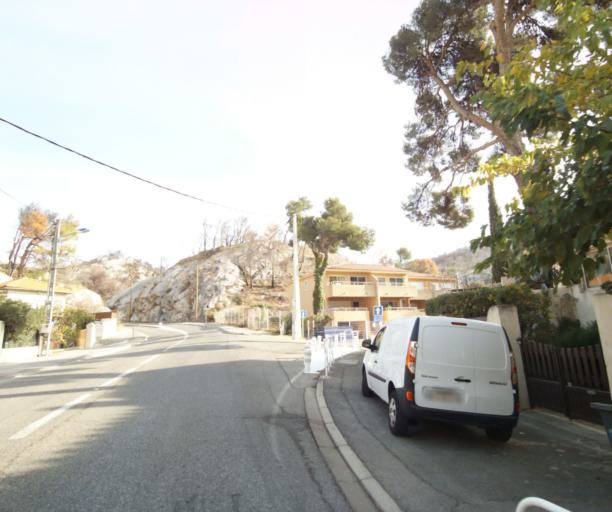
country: FR
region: Provence-Alpes-Cote d'Azur
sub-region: Departement des Bouches-du-Rhone
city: Carry-le-Rouet
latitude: 43.3369
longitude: 5.1772
